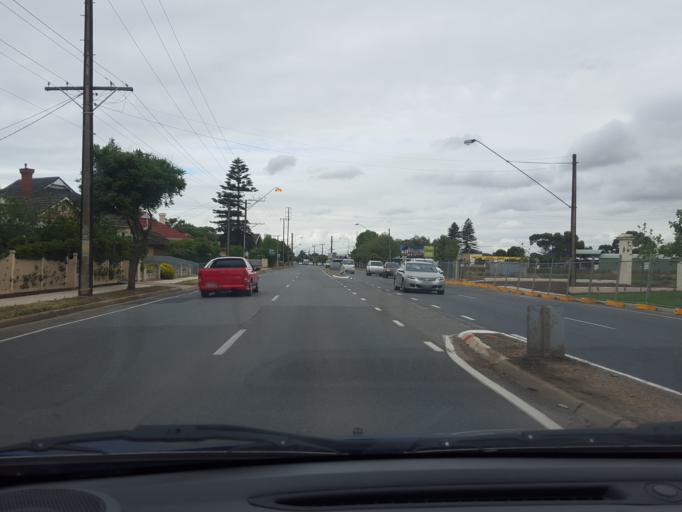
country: AU
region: South Australia
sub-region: Port Adelaide Enfield
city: Alberton
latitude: -34.8662
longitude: 138.5291
